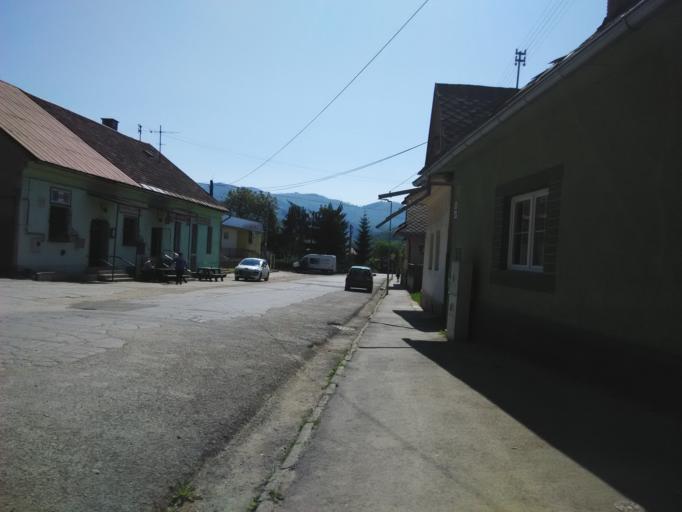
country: SK
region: Kosicky
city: Dobsina
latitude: 48.8214
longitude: 20.3577
